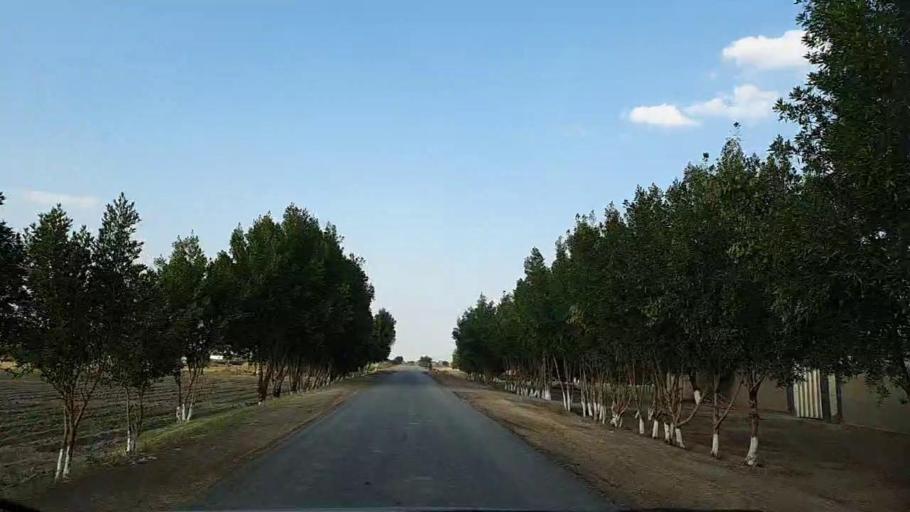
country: PK
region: Sindh
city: Pithoro
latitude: 25.6883
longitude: 69.2220
